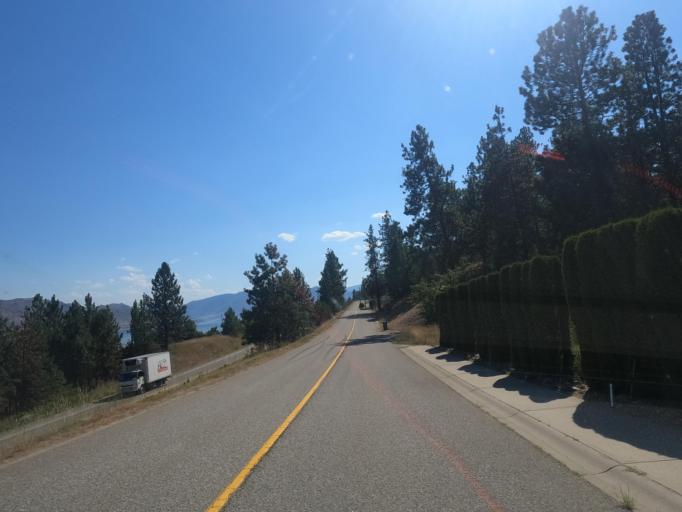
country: CA
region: British Columbia
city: Peachland
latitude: 49.7915
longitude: -119.7064
